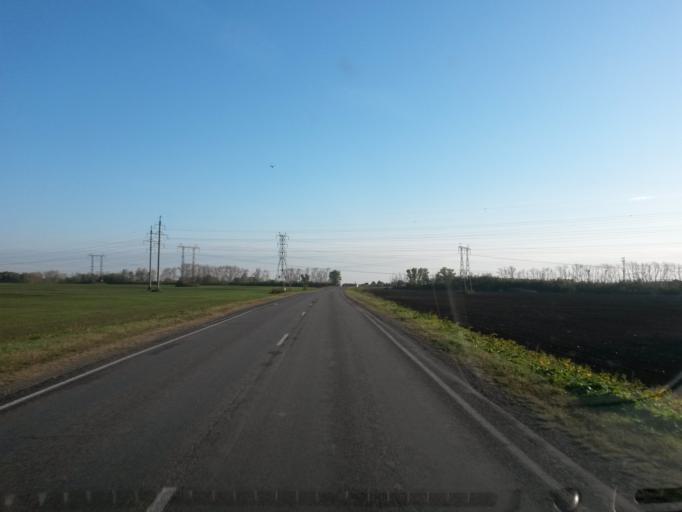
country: RU
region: Moskovskaya
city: Barybino
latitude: 55.2559
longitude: 37.8262
